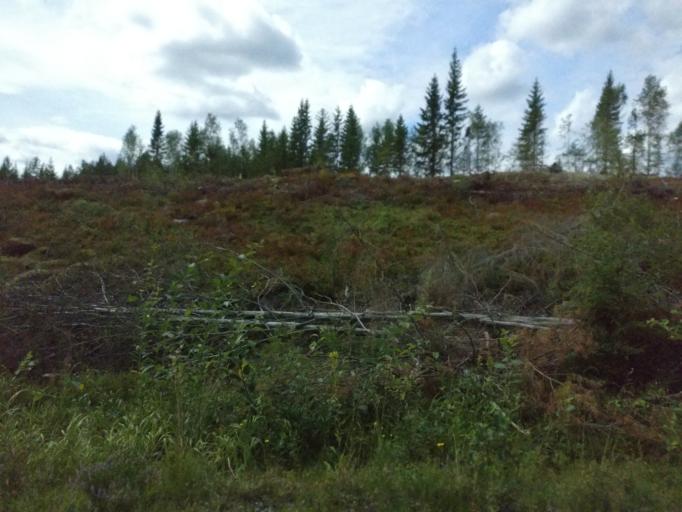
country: SE
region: Vaermland
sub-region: Hagfors Kommun
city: Hagfors
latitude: 60.0173
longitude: 13.7304
